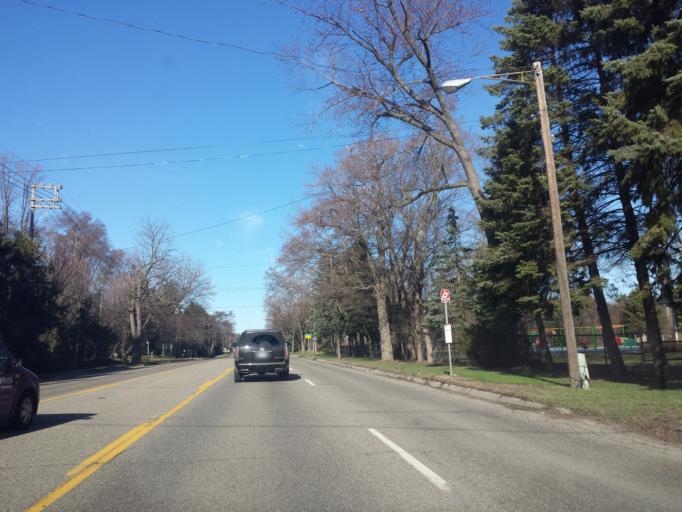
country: US
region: Michigan
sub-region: Oakland County
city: Franklin
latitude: 42.5446
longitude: -83.2971
